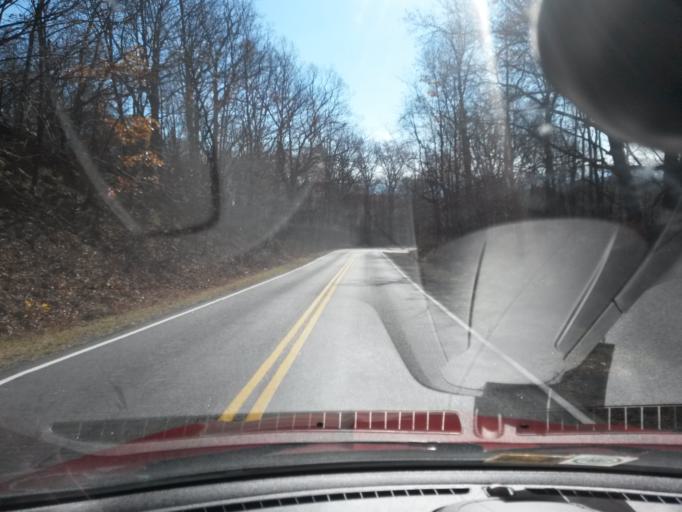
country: US
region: Virginia
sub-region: City of Bedford
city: Bedford
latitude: 37.4391
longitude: -79.5856
